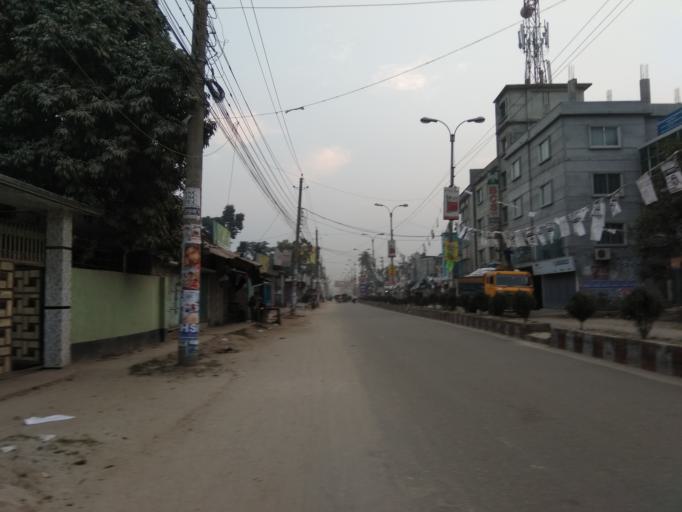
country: BD
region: Rangpur Division
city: Rangpur
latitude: 25.7377
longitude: 89.2548
